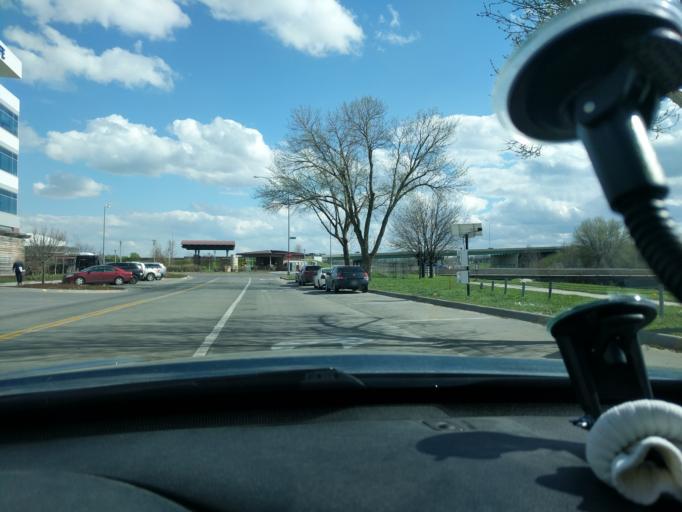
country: US
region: Nebraska
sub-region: Douglas County
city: Ralston
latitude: 41.2389
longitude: -96.0168
